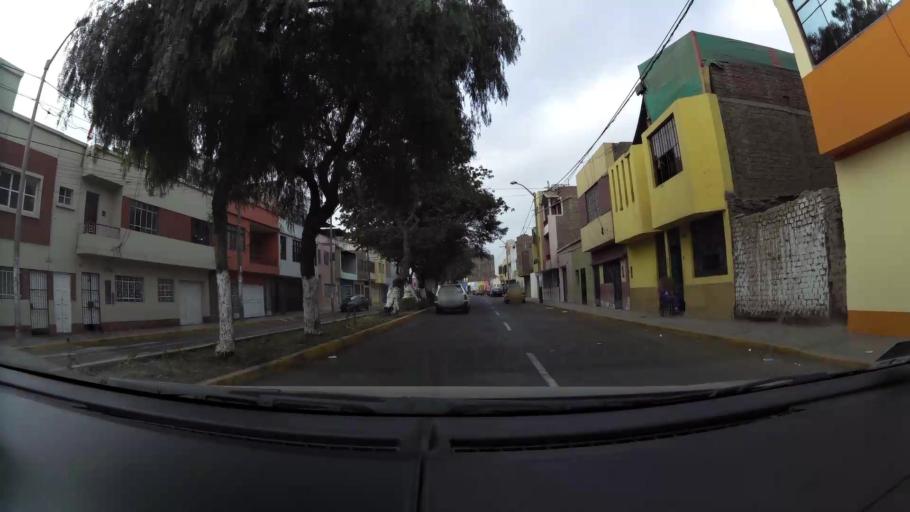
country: PE
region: La Libertad
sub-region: Provincia de Trujillo
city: Trujillo
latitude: -8.1011
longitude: -79.0181
